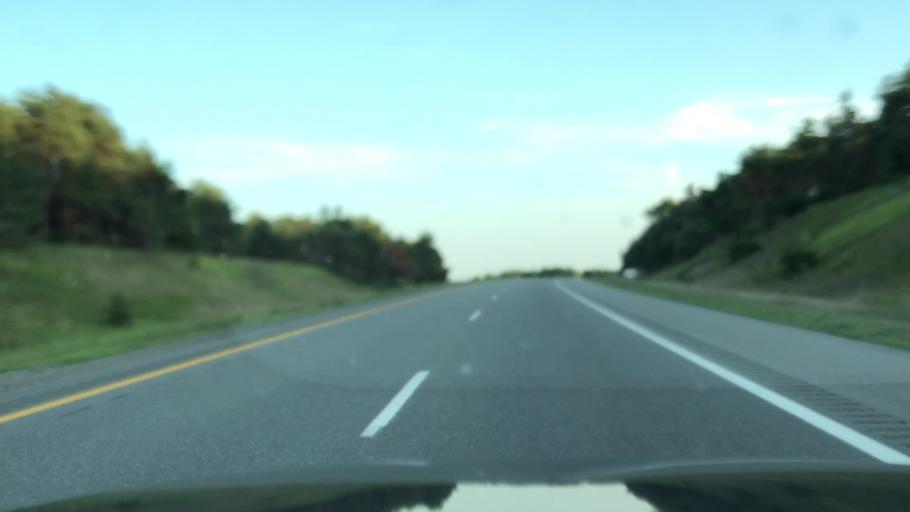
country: US
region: Michigan
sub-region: Osceola County
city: Reed City
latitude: 43.8506
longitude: -85.5324
